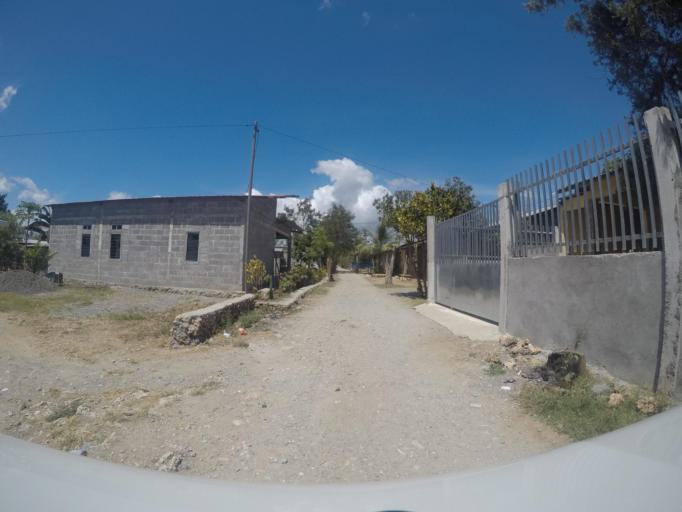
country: TL
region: Baucau
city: Baucau
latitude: -8.4832
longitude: 126.4512
